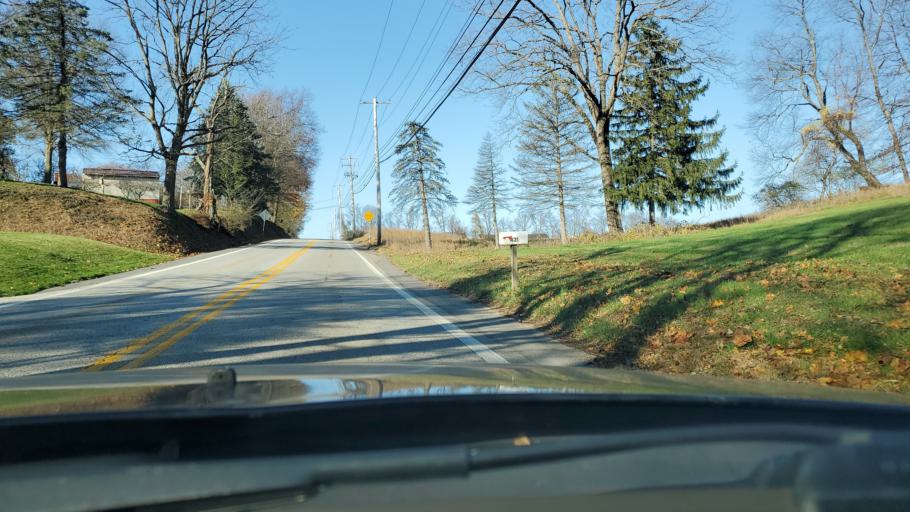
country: US
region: Pennsylvania
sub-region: Cumberland County
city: Mechanicsburg
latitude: 40.1629
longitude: -76.9925
